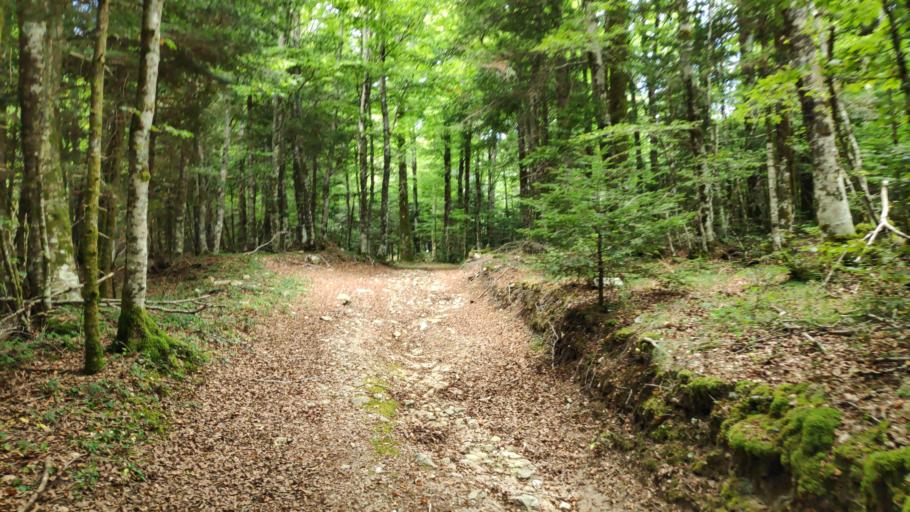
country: IT
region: Calabria
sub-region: Provincia di Vibo-Valentia
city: Serra San Bruno
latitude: 38.5425
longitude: 16.3648
